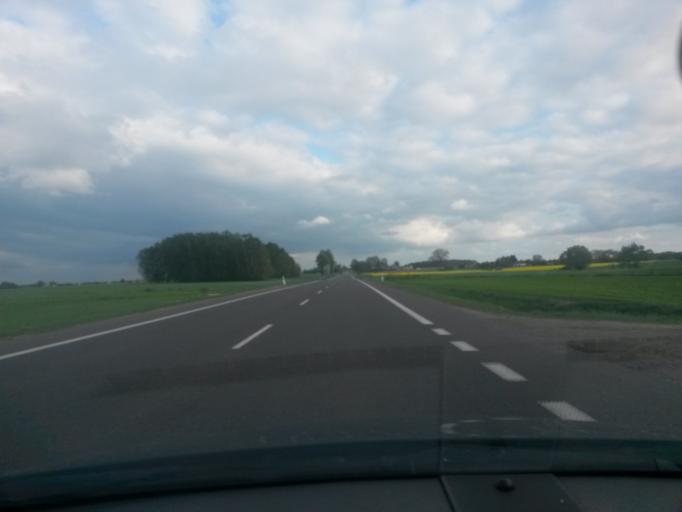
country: PL
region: Masovian Voivodeship
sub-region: Powiat plocki
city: Drobin
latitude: 52.6994
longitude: 20.0406
